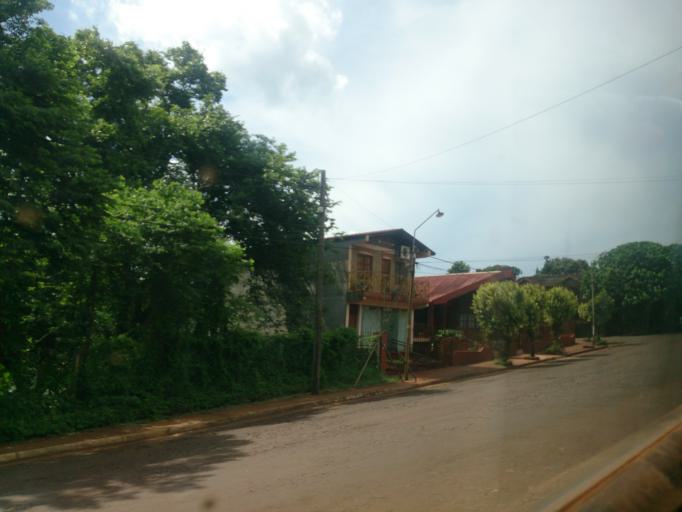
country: AR
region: Misiones
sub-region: Departamento de Obera
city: Obera
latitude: -27.4914
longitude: -55.1145
